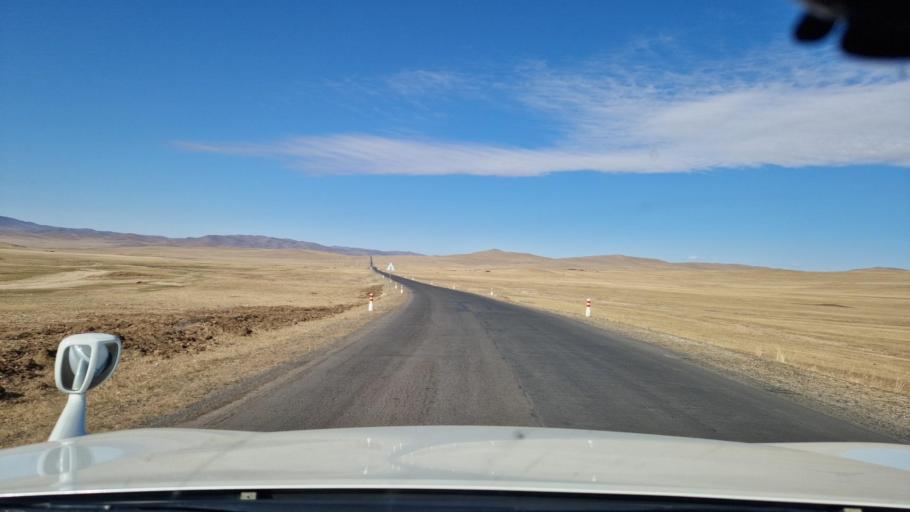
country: MN
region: Hentiy
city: Modot
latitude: 47.5952
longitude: 109.2525
